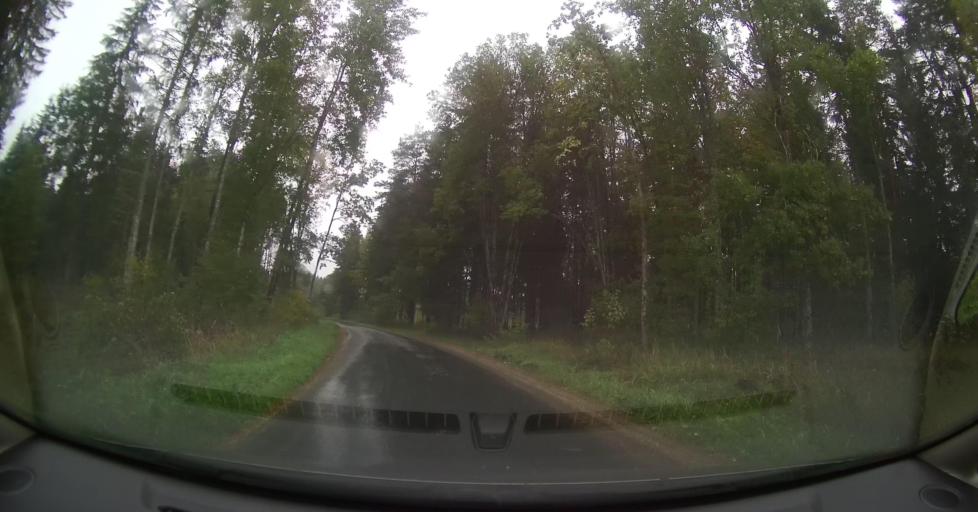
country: EE
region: Tartu
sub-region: UElenurme vald
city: Ulenurme
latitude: 58.3470
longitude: 26.8070
